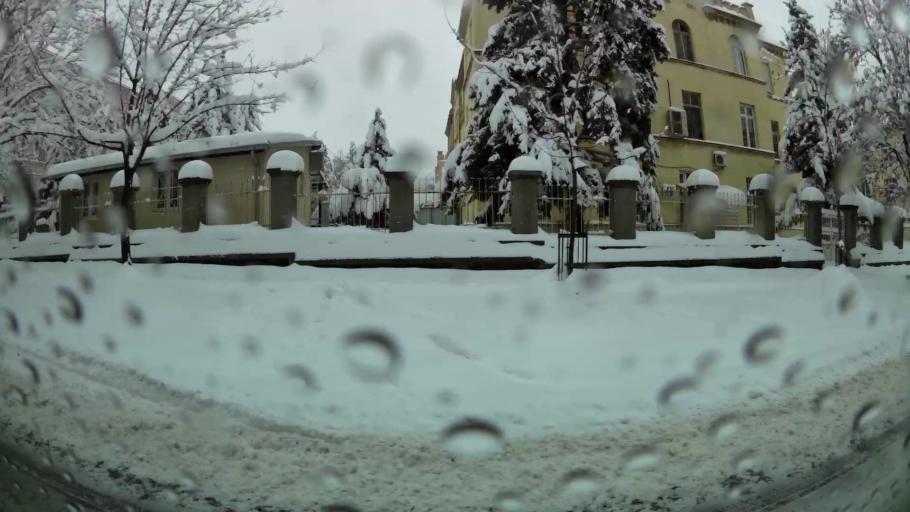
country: RS
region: Central Serbia
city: Belgrade
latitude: 44.7998
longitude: 20.4617
